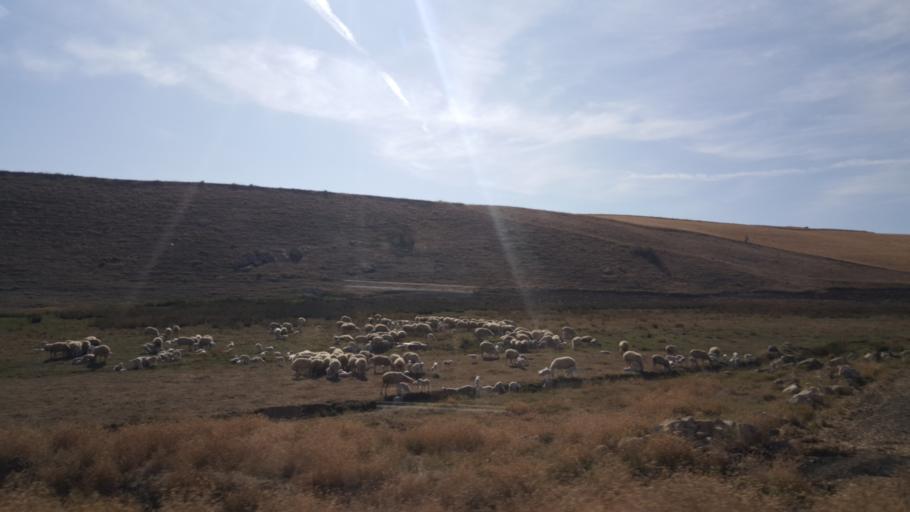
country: TR
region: Ankara
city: Haymana
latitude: 39.4206
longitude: 32.5923
